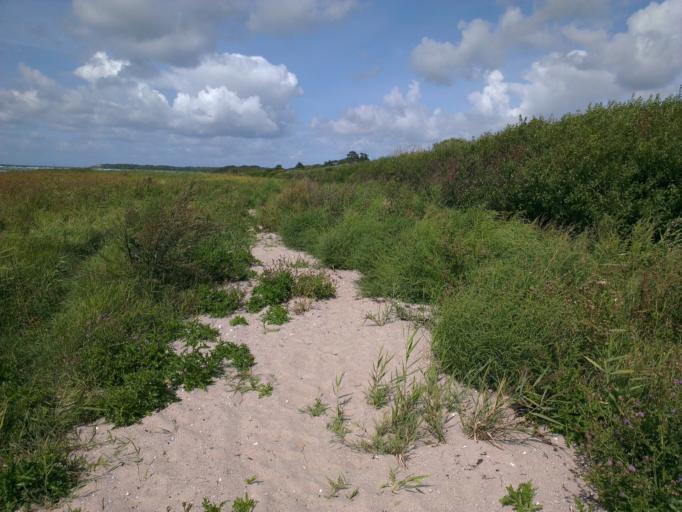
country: DK
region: Capital Region
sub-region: Frederikssund Kommune
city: Jaegerspris
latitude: 55.8542
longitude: 11.9586
